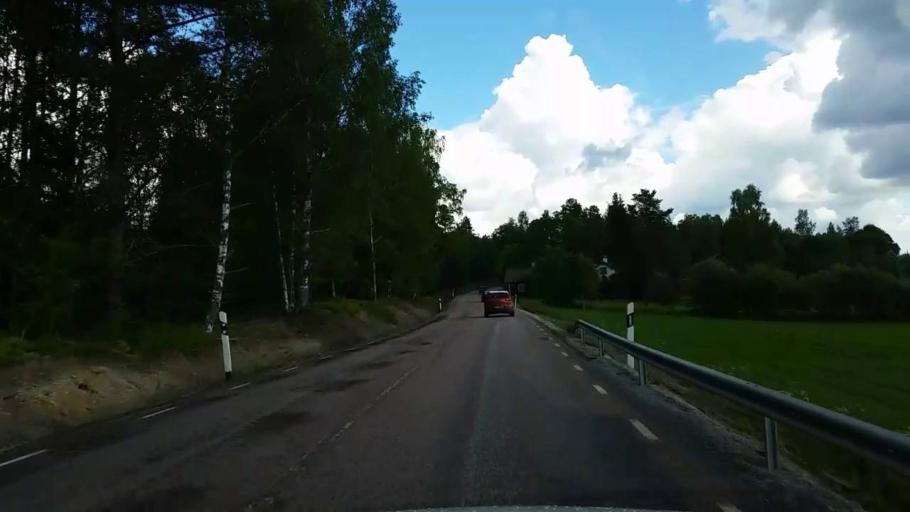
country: SE
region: Vaestmanland
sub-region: Skinnskattebergs Kommun
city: Skinnskatteberg
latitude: 59.8559
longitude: 15.8417
